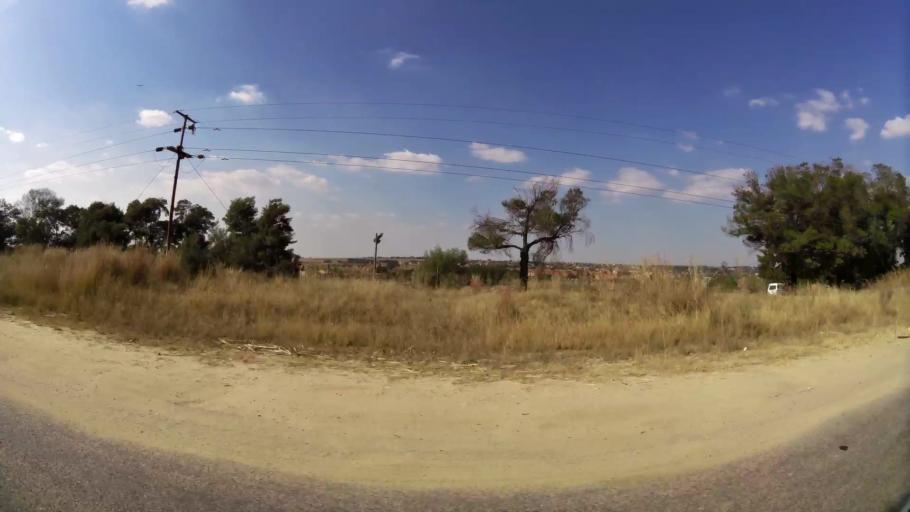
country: ZA
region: Gauteng
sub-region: Ekurhuleni Metropolitan Municipality
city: Tembisa
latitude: -26.0529
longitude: 28.2480
